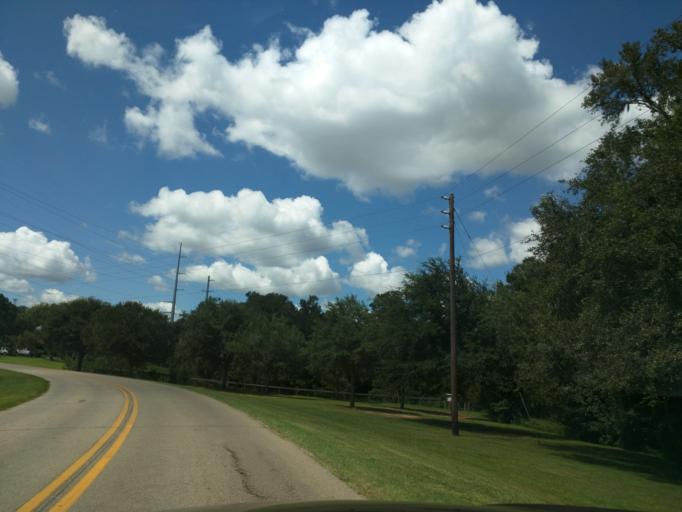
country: US
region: Florida
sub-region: Leon County
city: Tallahassee
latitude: 30.4500
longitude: -84.2171
